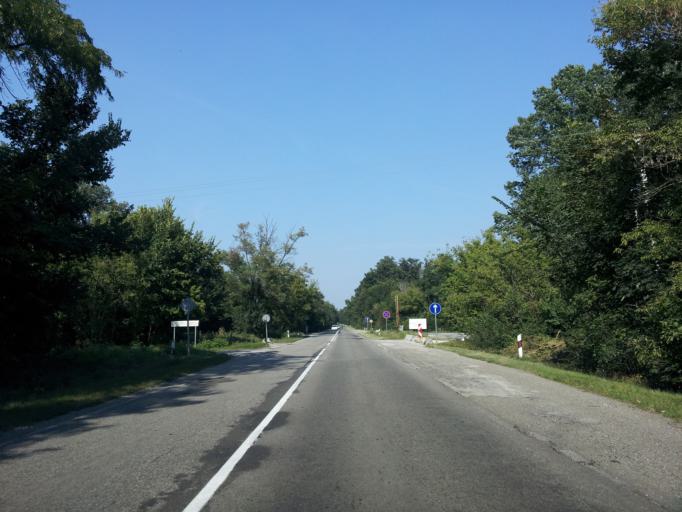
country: HU
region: Fejer
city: Polgardi
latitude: 47.0230
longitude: 18.2826
